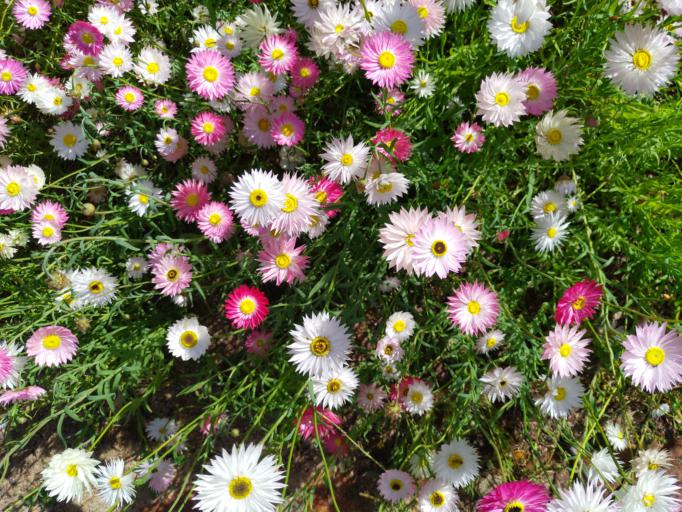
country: AU
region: Western Australia
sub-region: City of Perth
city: West Perth
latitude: -31.9668
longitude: 115.8376
